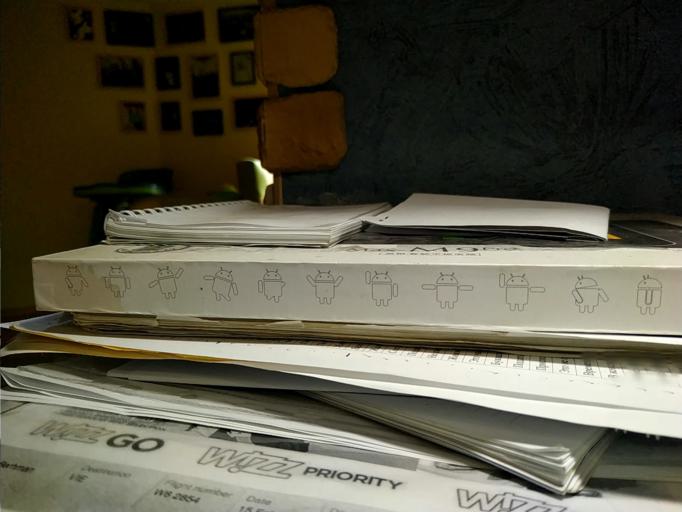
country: RU
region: Novgorod
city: Poddor'ye
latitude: 57.4536
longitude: 31.0106
